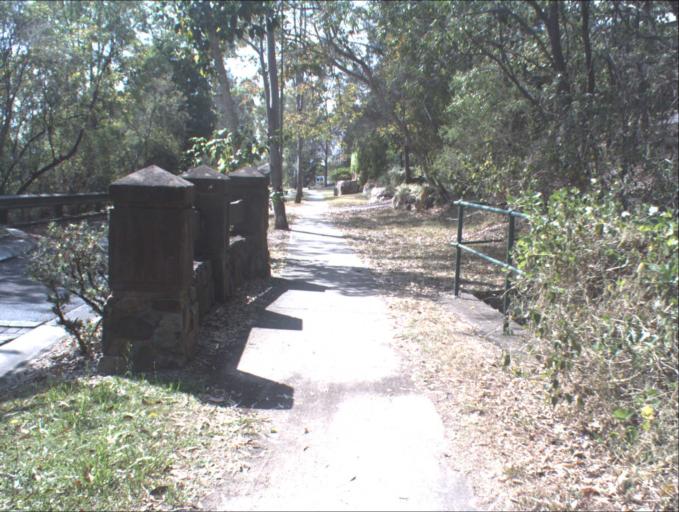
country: AU
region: Queensland
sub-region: Logan
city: Slacks Creek
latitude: -27.6562
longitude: 153.1948
